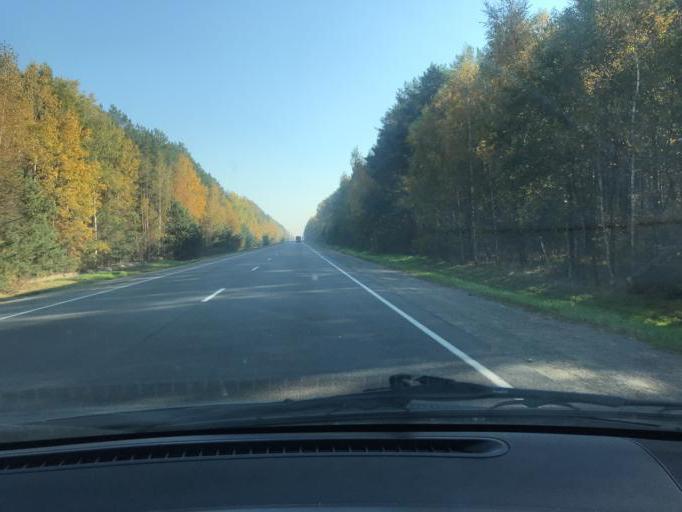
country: BY
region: Brest
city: Luninyets
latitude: 52.2774
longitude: 26.8493
